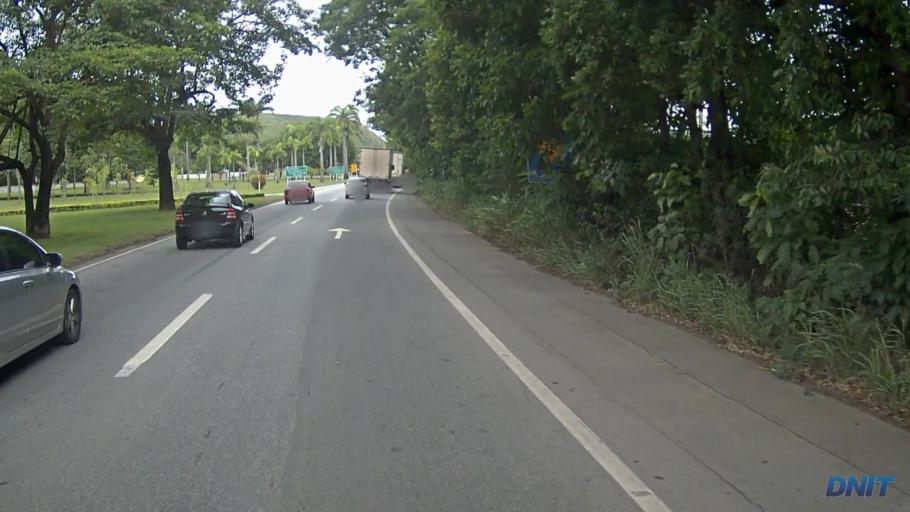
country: BR
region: Minas Gerais
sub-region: Ipatinga
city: Ipatinga
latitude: -19.4877
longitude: -42.5588
